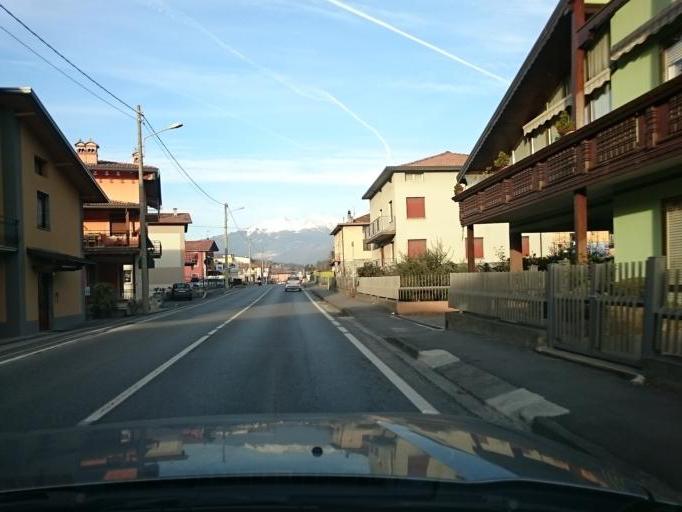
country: IT
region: Lombardy
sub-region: Provincia di Brescia
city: Losine
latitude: 45.9772
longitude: 10.3219
